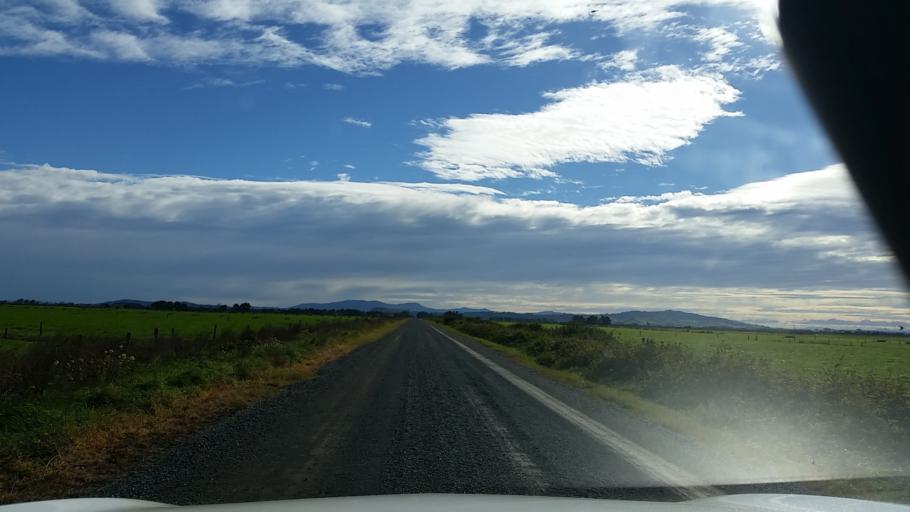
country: NZ
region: Waikato
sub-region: Hamilton City
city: Hamilton
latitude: -37.6858
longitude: 175.4451
